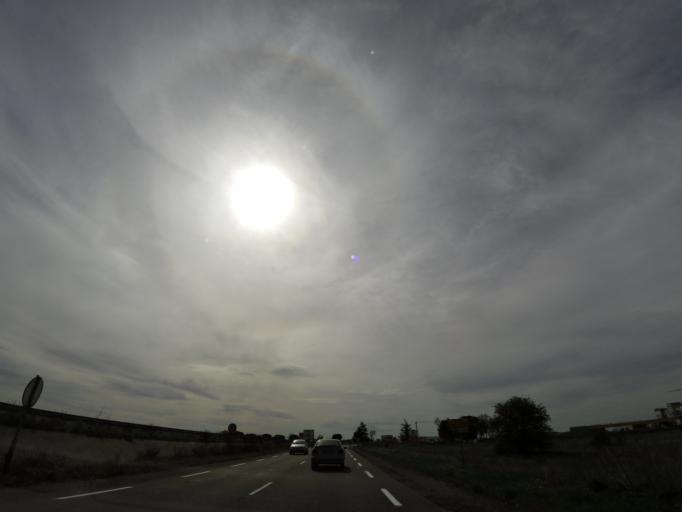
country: FR
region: Languedoc-Roussillon
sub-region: Departement du Gard
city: Gallargues-le-Montueux
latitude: 43.7085
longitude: 4.1892
